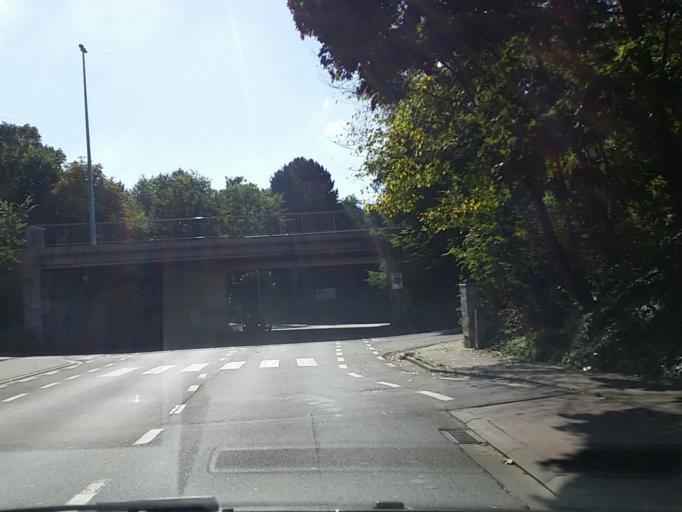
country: BE
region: Flanders
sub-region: Provincie Vlaams-Brabant
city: Leuven
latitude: 50.8898
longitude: 4.6946
